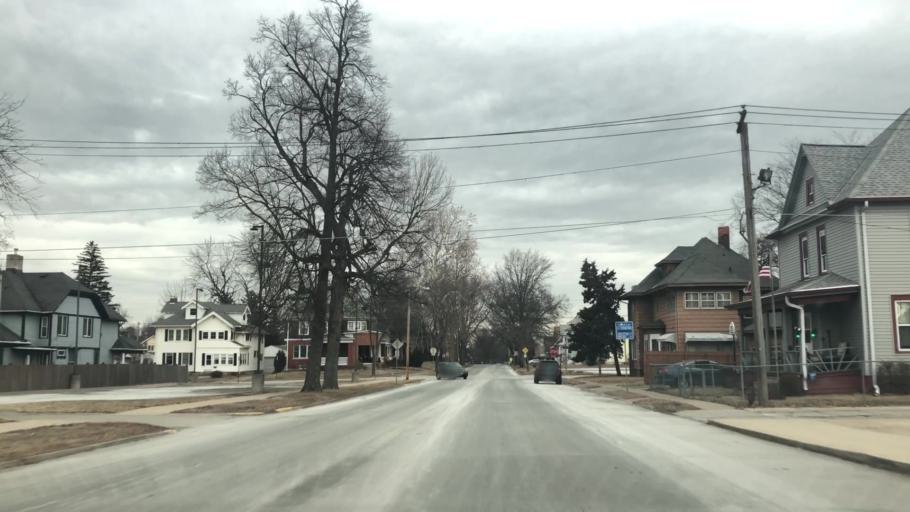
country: US
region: Iowa
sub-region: Marshall County
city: Marshalltown
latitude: 42.0495
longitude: -92.9179
